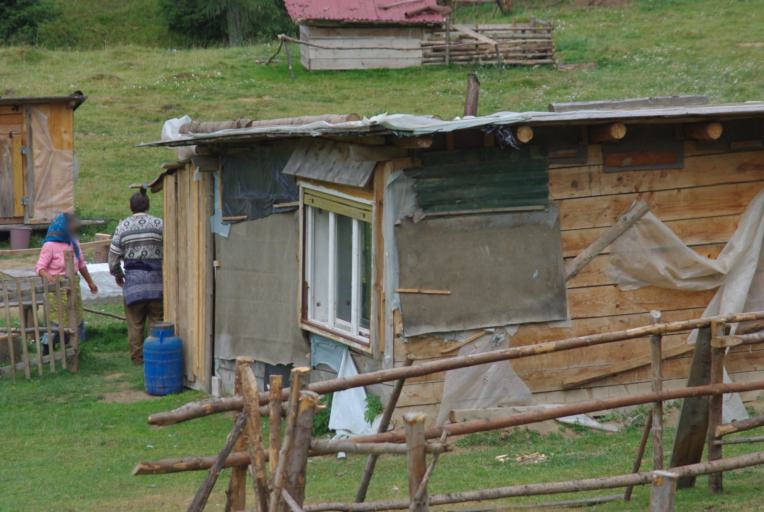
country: RO
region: Alba
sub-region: Comuna Arieseni
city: Arieseni
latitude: 46.5895
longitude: 22.6864
